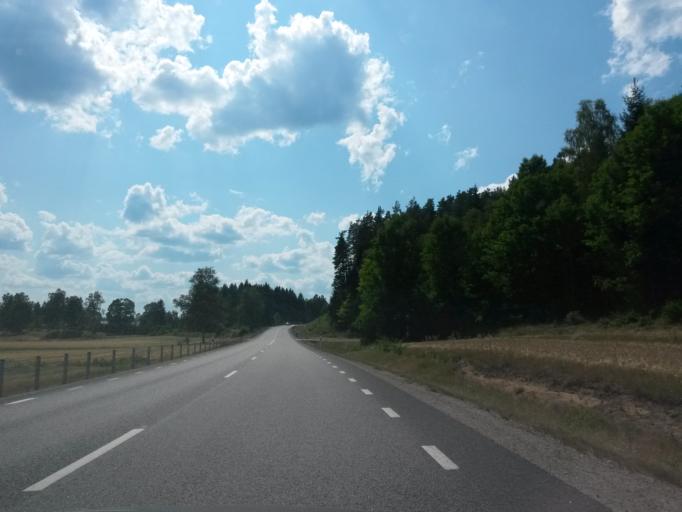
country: SE
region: Vaestra Goetaland
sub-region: Vargarda Kommun
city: Vargarda
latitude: 58.0527
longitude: 12.8951
